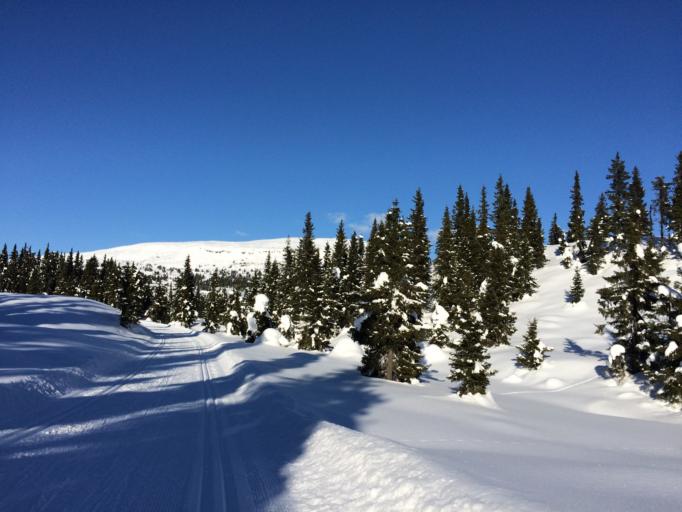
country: NO
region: Oppland
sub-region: Gausdal
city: Segalstad bru
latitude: 61.3354
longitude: 10.0605
